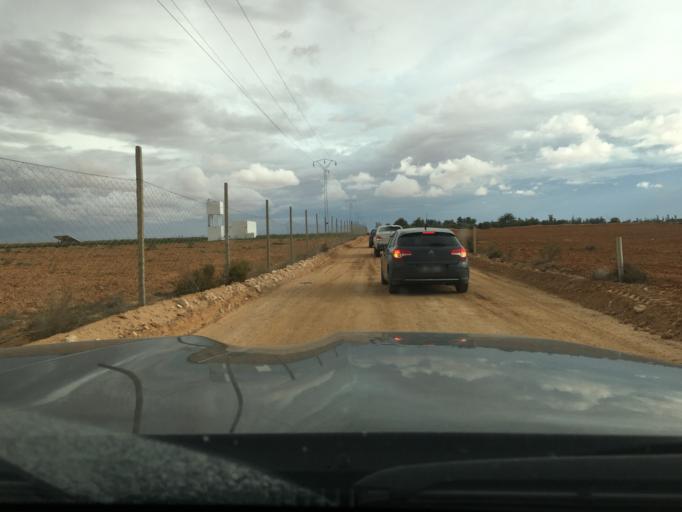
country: TN
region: Madanin
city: Medenine
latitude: 33.2774
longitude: 10.5593
